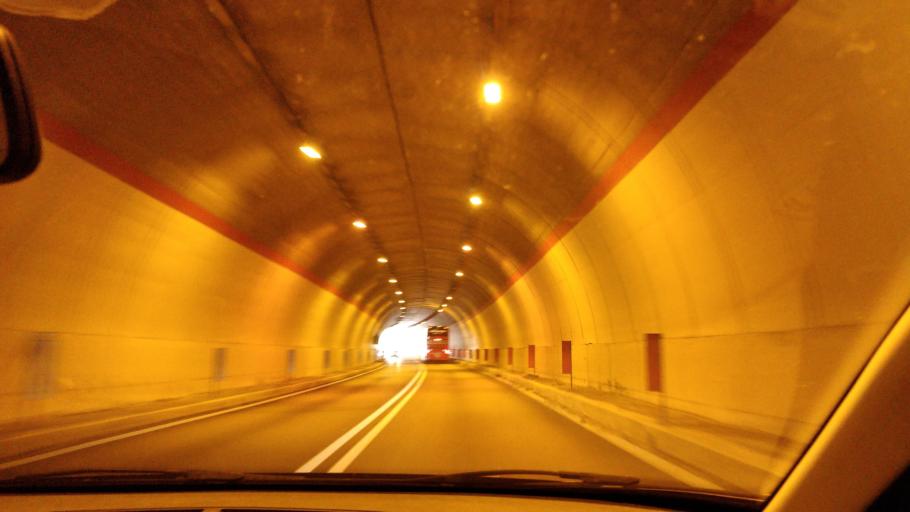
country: IT
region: Abruzzo
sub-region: Provincia di Chieti
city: Francavilla al Mare
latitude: 42.4013
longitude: 14.2991
